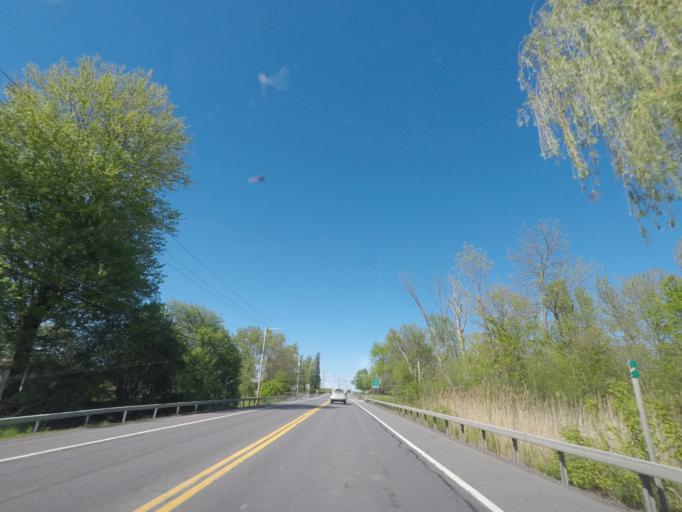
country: US
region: New York
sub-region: Greene County
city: Coxsackie
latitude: 42.3548
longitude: -73.8381
